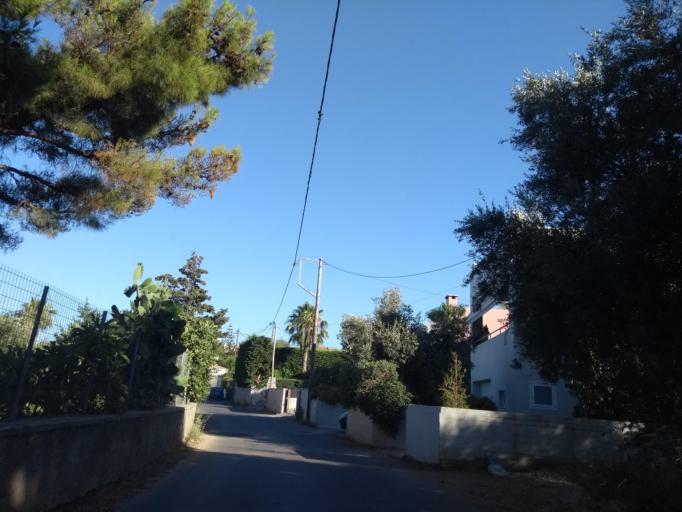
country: GR
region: Crete
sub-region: Nomos Chanias
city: Pithari
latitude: 35.5209
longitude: 24.0780
